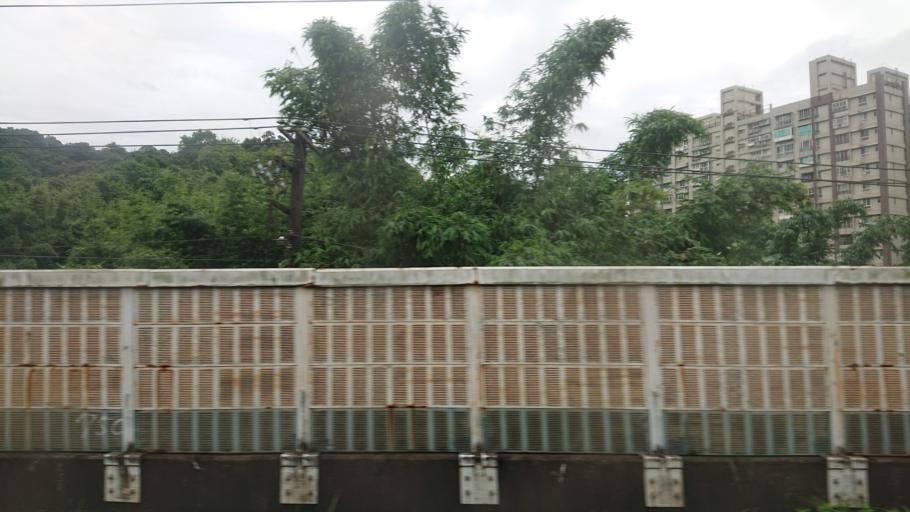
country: TW
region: Taiwan
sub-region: Keelung
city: Keelung
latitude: 25.0824
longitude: 121.6759
